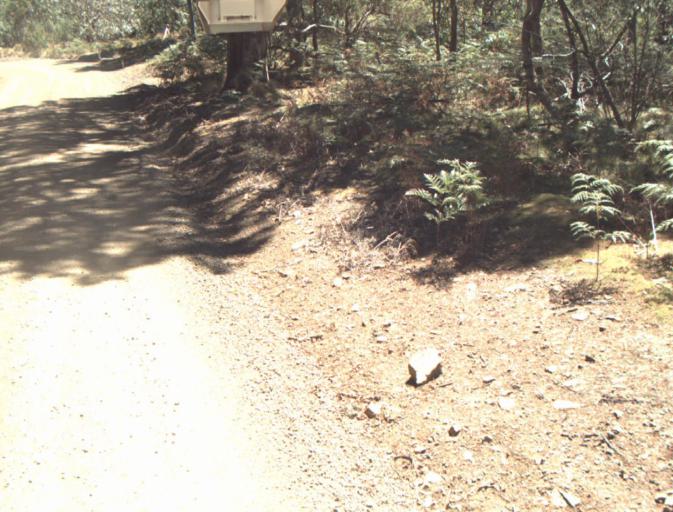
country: AU
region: Tasmania
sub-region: Dorset
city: Scottsdale
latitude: -41.3540
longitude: 147.4247
